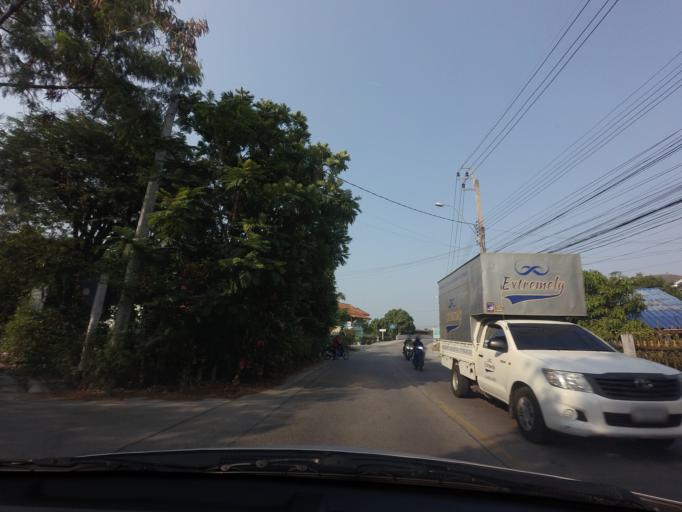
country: TH
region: Nonthaburi
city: Bang Yai
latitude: 13.8061
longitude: 100.3961
